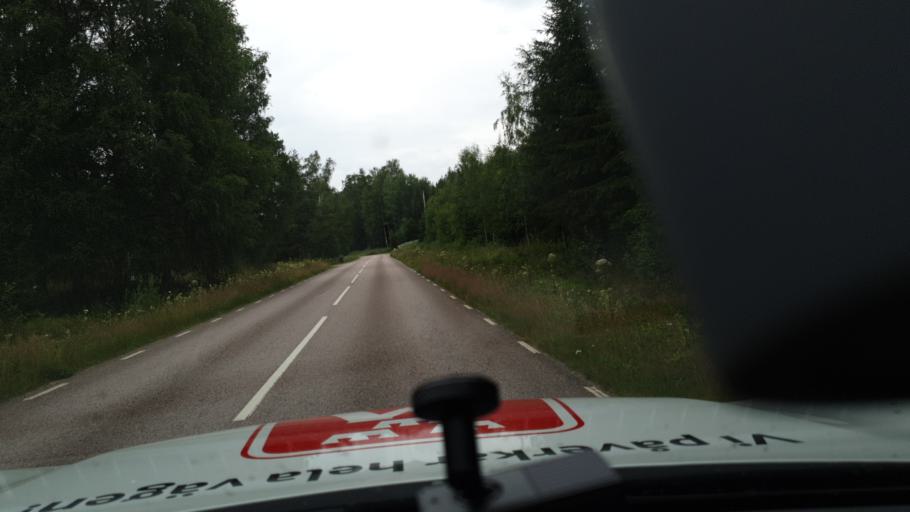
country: SE
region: Vaermland
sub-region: Sunne Kommun
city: Sunne
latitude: 59.7697
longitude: 13.2385
